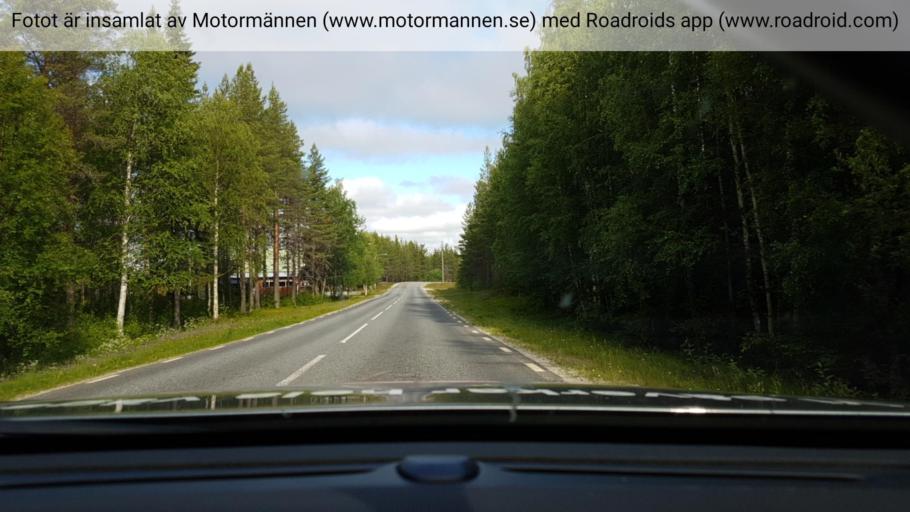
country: SE
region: Vaesterbotten
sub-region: Norsjo Kommun
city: Norsjoe
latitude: 64.7112
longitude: 19.1487
